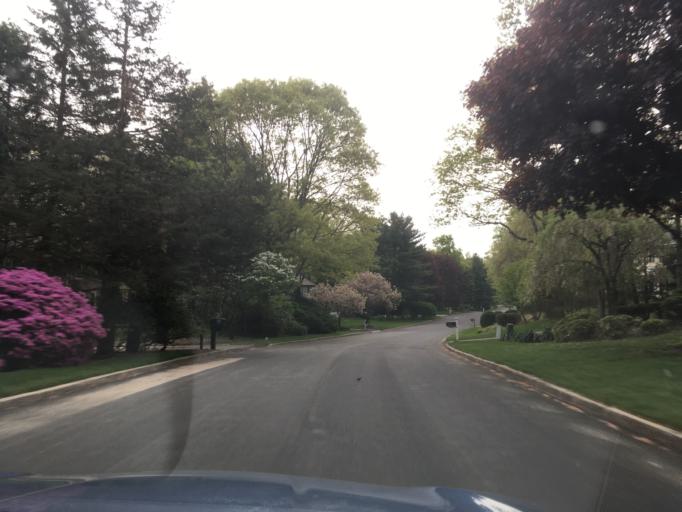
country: US
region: Rhode Island
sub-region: Kent County
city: West Warwick
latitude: 41.6581
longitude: -71.5120
